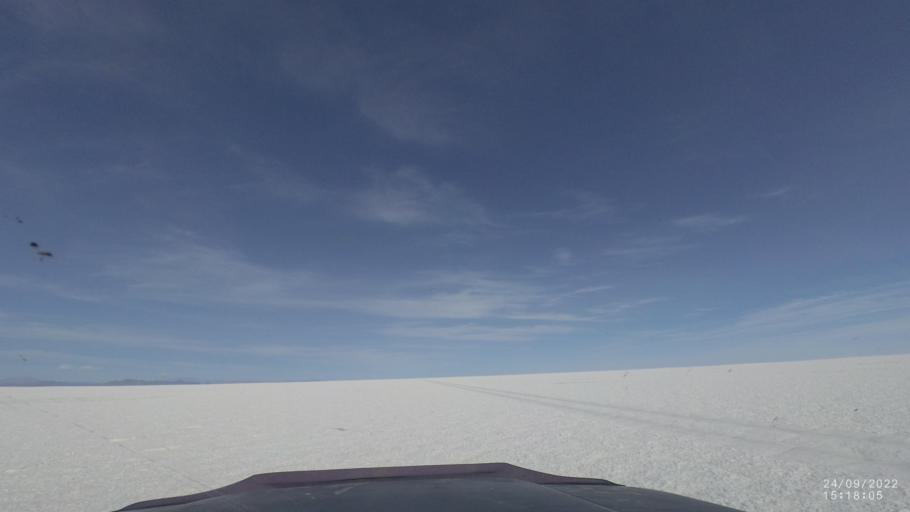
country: BO
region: Potosi
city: Colchani
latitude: -19.9944
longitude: -67.4215
